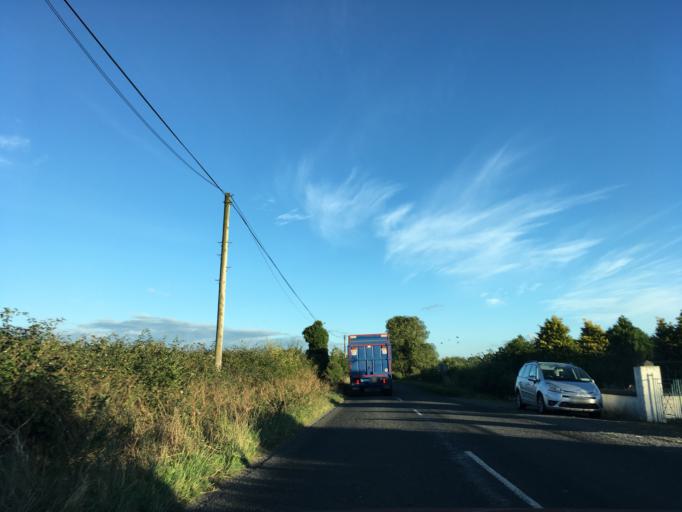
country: IE
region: Munster
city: Cashel
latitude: 52.4651
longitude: -7.9188
